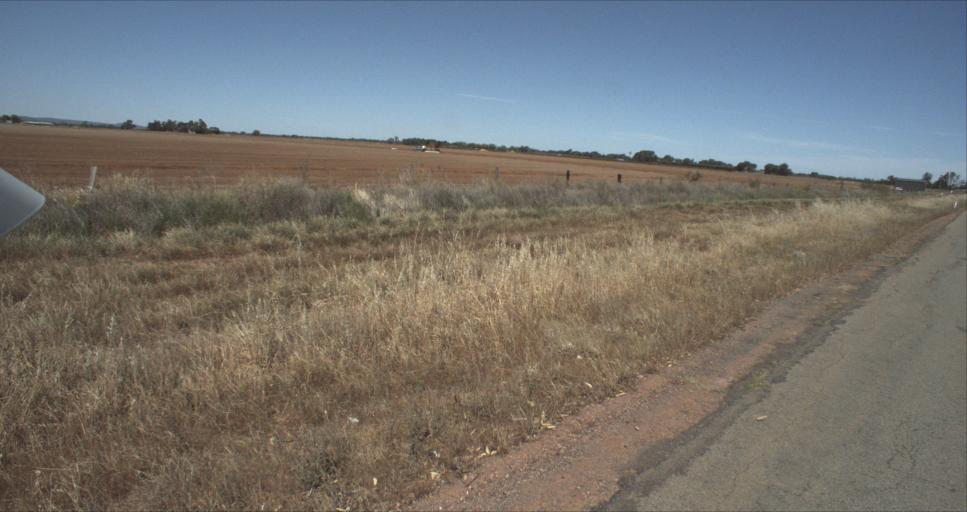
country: AU
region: New South Wales
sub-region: Leeton
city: Leeton
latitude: -34.5190
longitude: 146.3455
